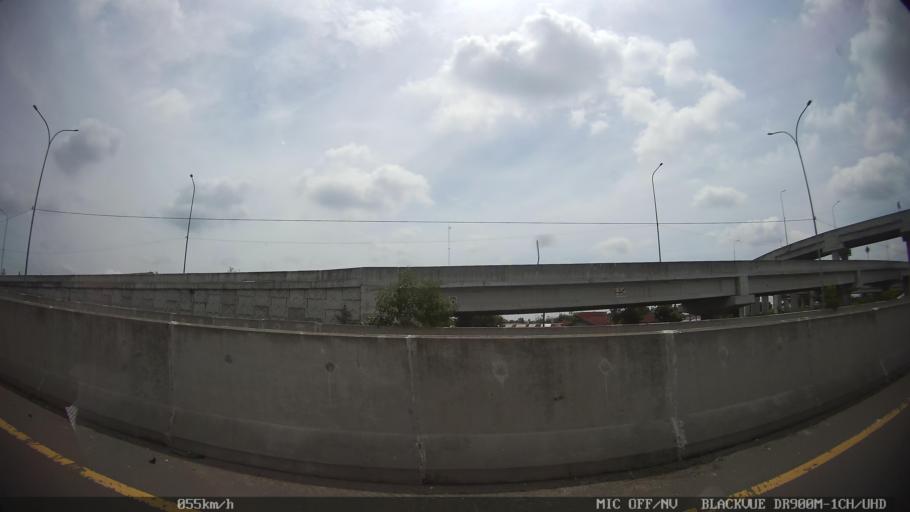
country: ID
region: North Sumatra
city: Medan
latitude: 3.6523
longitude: 98.6819
